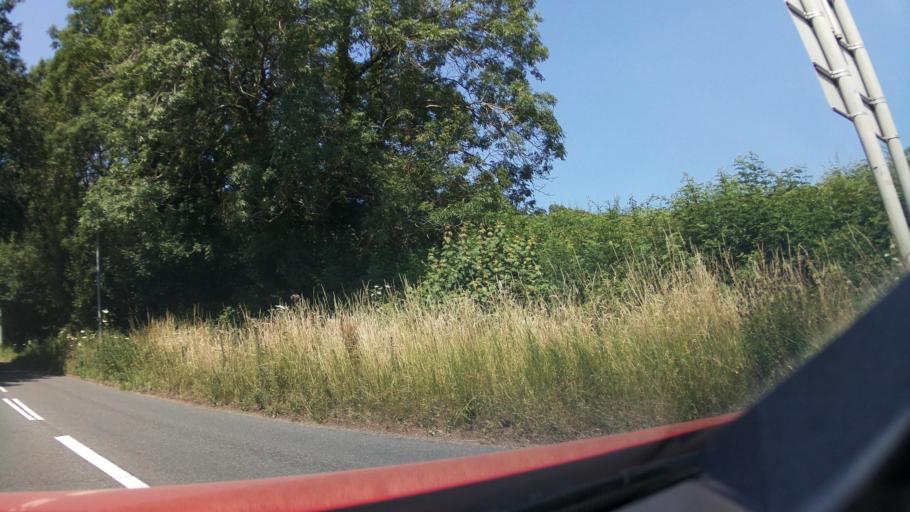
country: GB
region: Wales
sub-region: Caerphilly County Borough
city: Caerphilly
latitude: 51.5490
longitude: -3.2089
